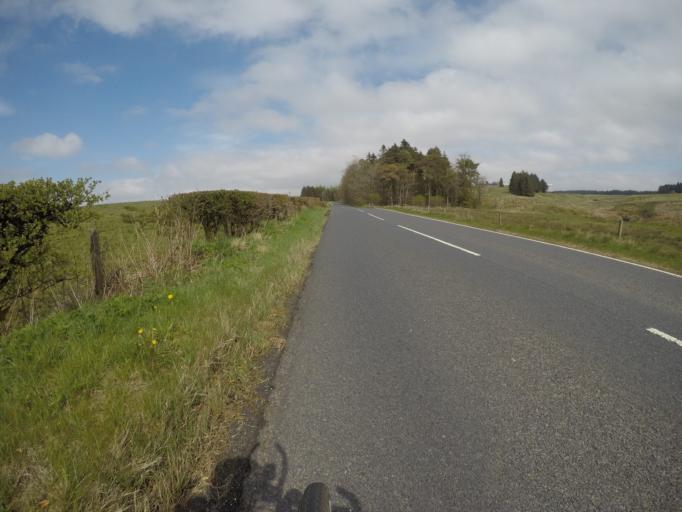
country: GB
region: Scotland
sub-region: East Renfrewshire
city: Neilston
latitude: 55.7182
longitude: -4.4351
